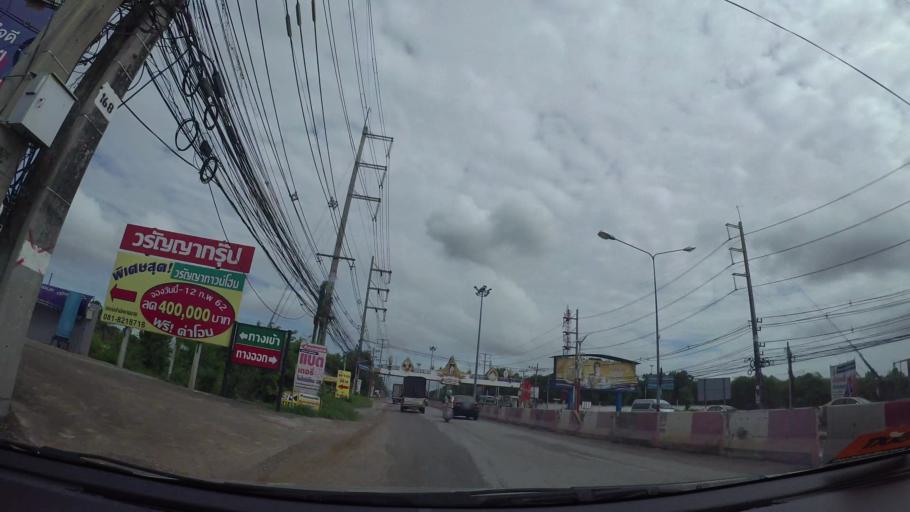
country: TH
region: Rayong
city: Rayong
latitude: 12.7035
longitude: 101.1844
